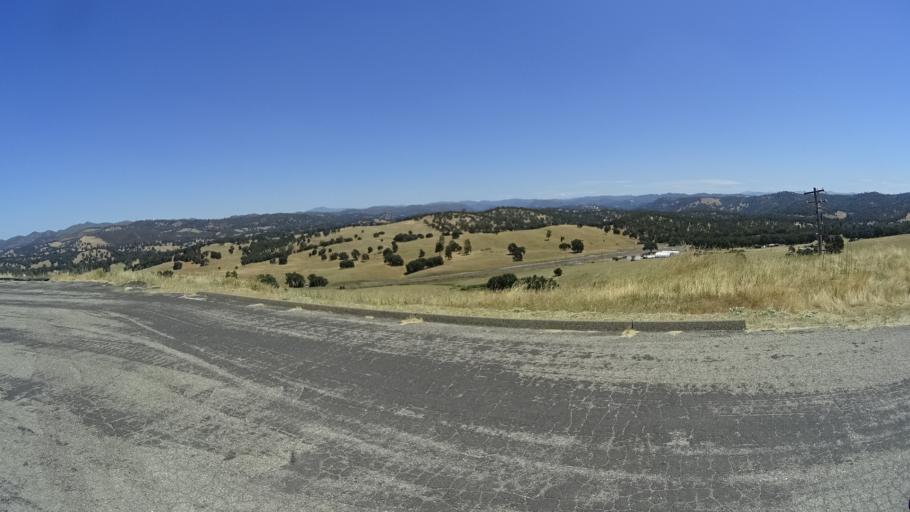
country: US
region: California
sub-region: Calaveras County
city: San Andreas
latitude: 38.1449
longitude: -120.6453
